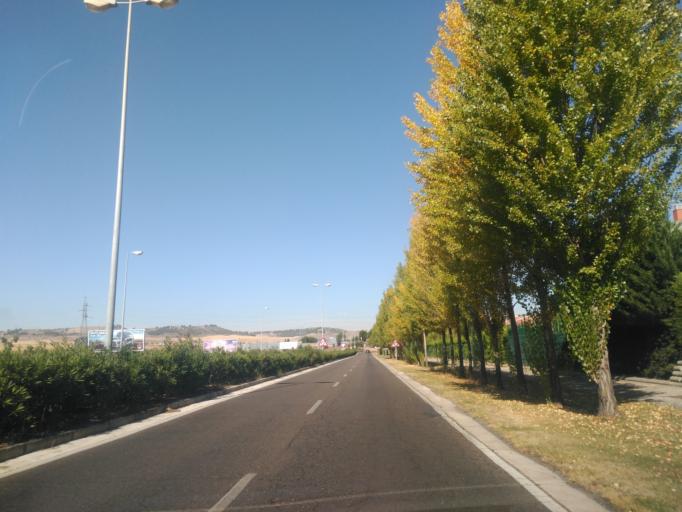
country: ES
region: Castille and Leon
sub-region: Provincia de Valladolid
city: Zaratan
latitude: 41.6325
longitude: -4.7712
